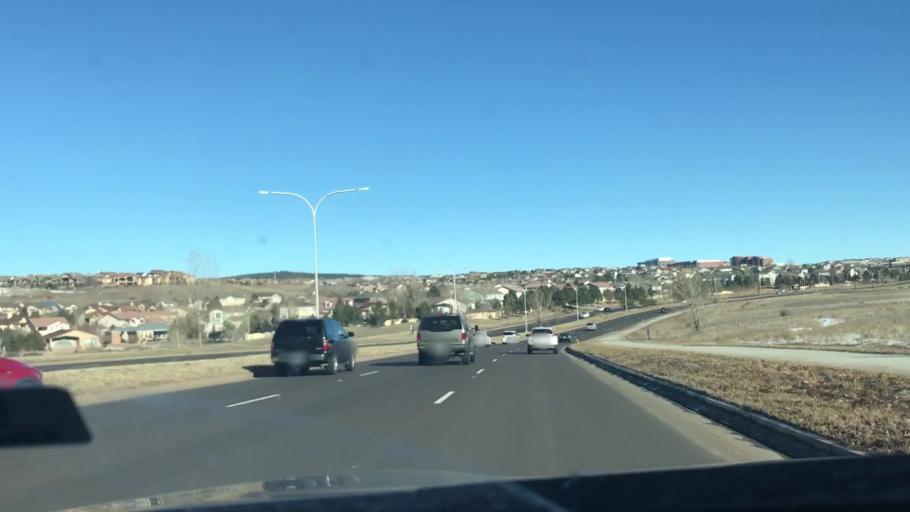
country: US
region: Colorado
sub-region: El Paso County
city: Black Forest
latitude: 38.9677
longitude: -104.7748
